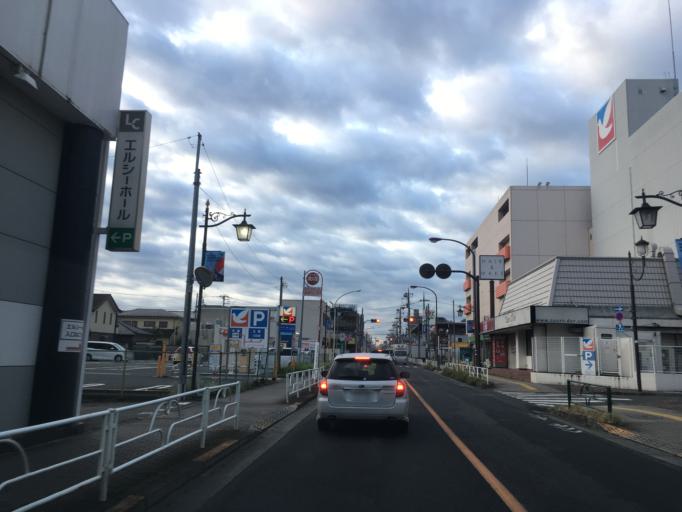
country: JP
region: Tokyo
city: Higashimurayama-shi
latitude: 35.7596
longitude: 139.4672
